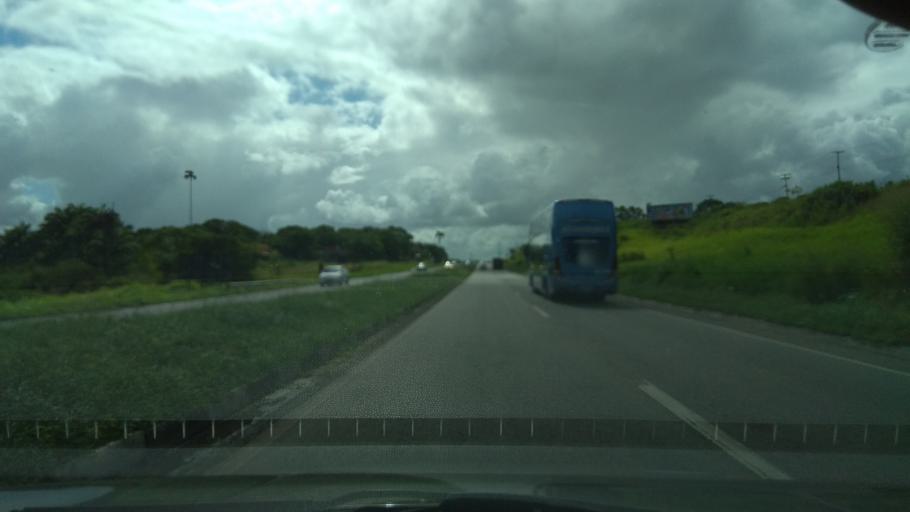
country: BR
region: Bahia
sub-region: Simoes Filho
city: Simoes Filho
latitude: -12.7750
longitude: -38.4181
